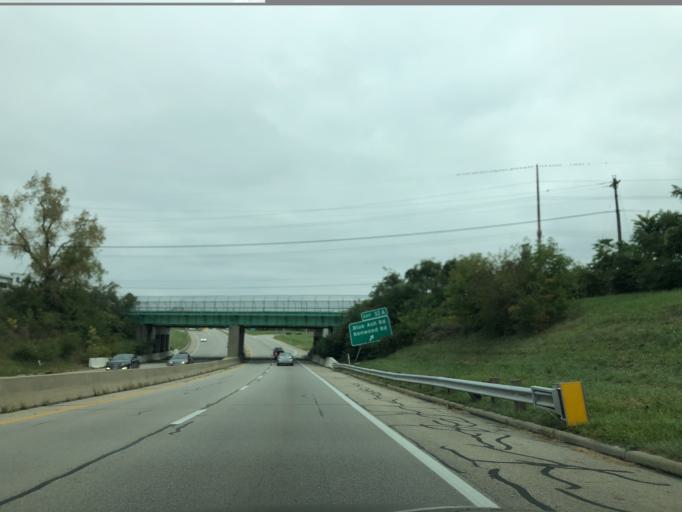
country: US
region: Ohio
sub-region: Hamilton County
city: Blue Ash
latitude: 39.2248
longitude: -84.3840
